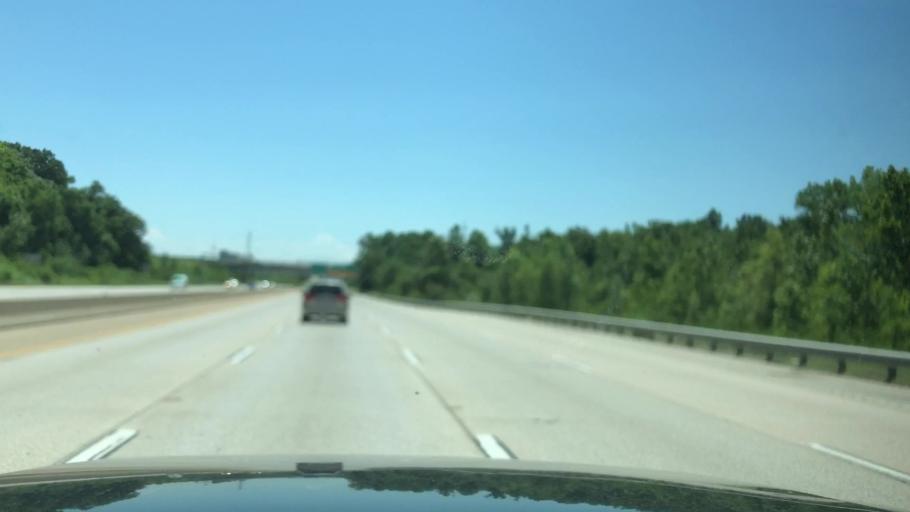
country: US
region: Missouri
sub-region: Saint Louis County
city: Bridgeton
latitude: 38.7776
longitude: -90.4146
